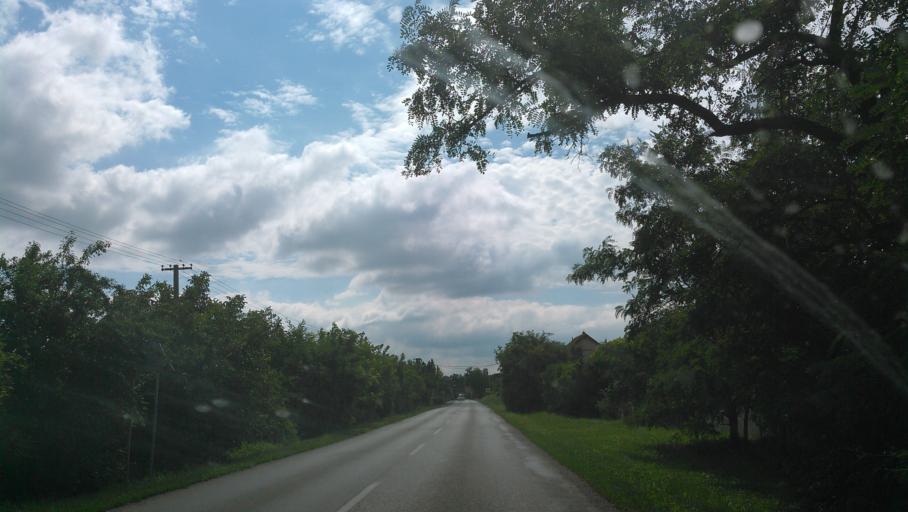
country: SK
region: Bratislavsky
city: Dunajska Luzna
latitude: 48.1544
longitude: 17.2869
